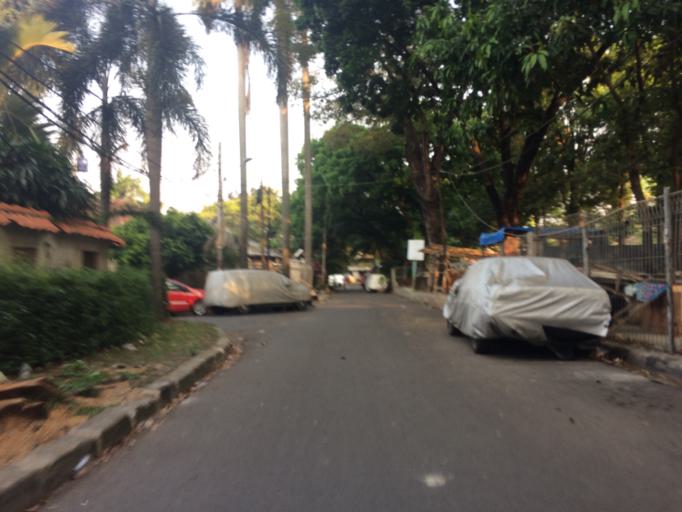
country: ID
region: Jakarta Raya
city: Jakarta
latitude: -6.2029
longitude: 106.8421
